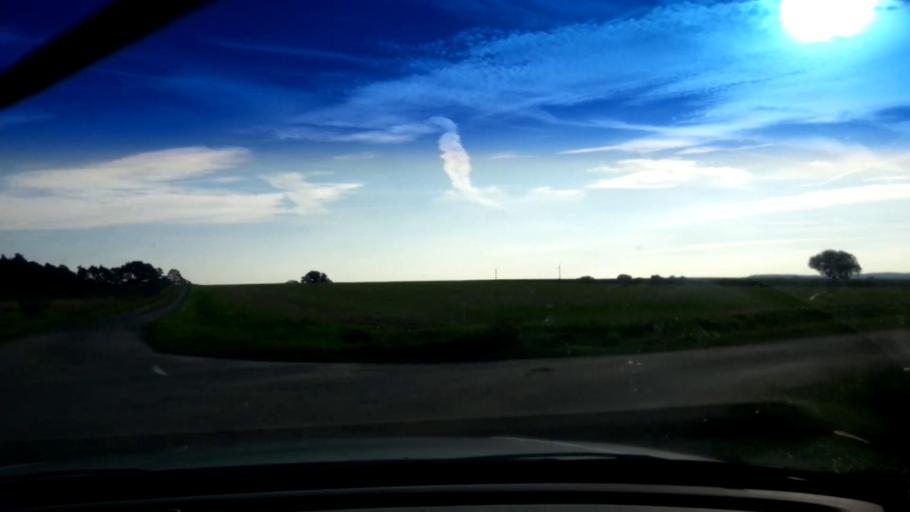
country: DE
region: Bavaria
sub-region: Upper Franconia
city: Lauter
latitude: 49.9482
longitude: 10.7739
